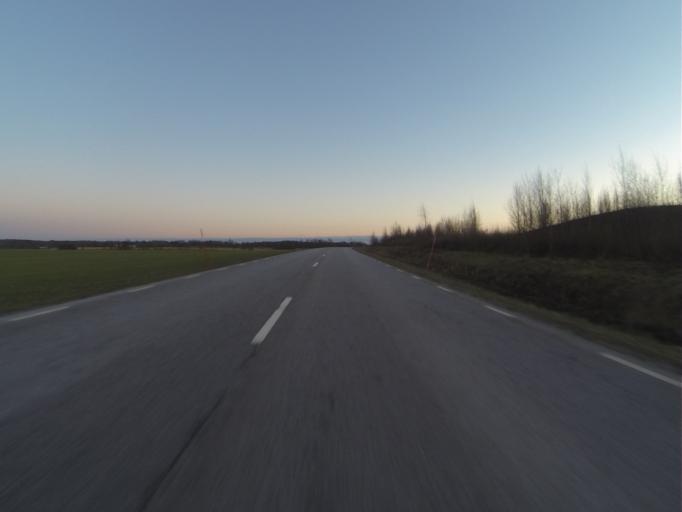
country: SE
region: Skane
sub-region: Lunds Kommun
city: Lund
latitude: 55.7058
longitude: 13.3021
